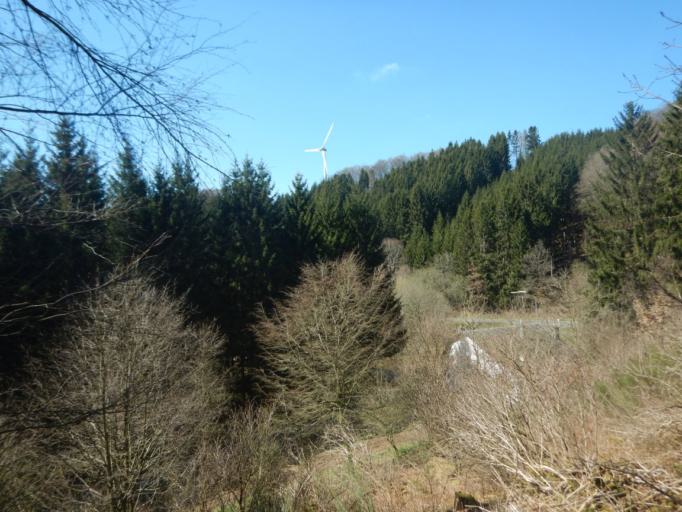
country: LU
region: Diekirch
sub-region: Canton de Clervaux
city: Weiswampach
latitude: 50.1067
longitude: 6.0436
